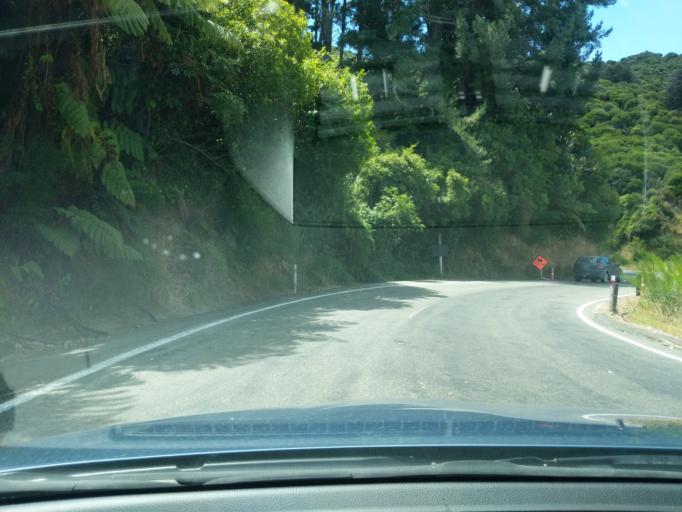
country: NZ
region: Tasman
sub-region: Tasman District
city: Motueka
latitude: -41.0491
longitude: 172.9595
